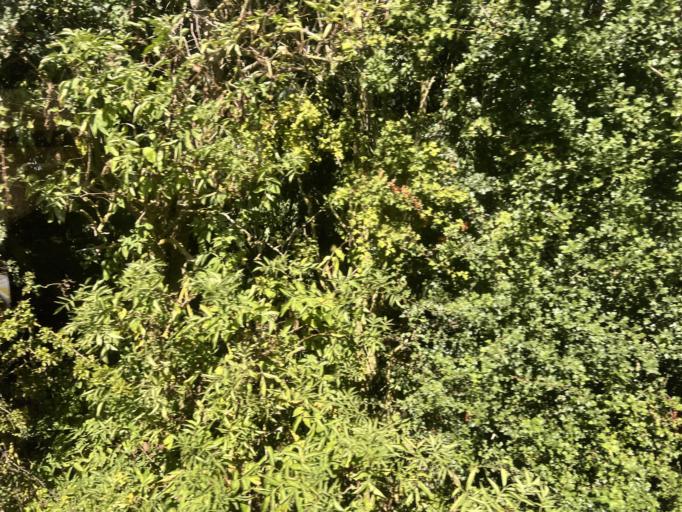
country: GB
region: England
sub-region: Lincolnshire
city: Spilsby
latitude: 53.0735
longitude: 0.0759
